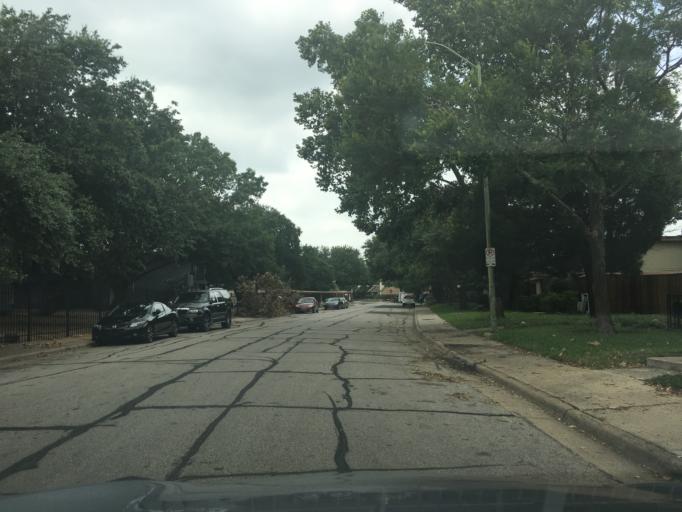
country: US
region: Texas
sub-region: Dallas County
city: Richardson
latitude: 32.9329
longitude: -96.7633
